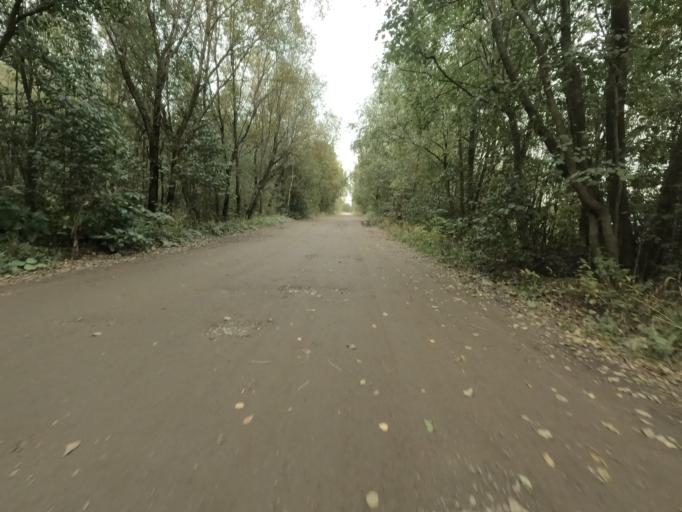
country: RU
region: St.-Petersburg
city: Sapernyy
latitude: 59.7606
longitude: 30.6537
